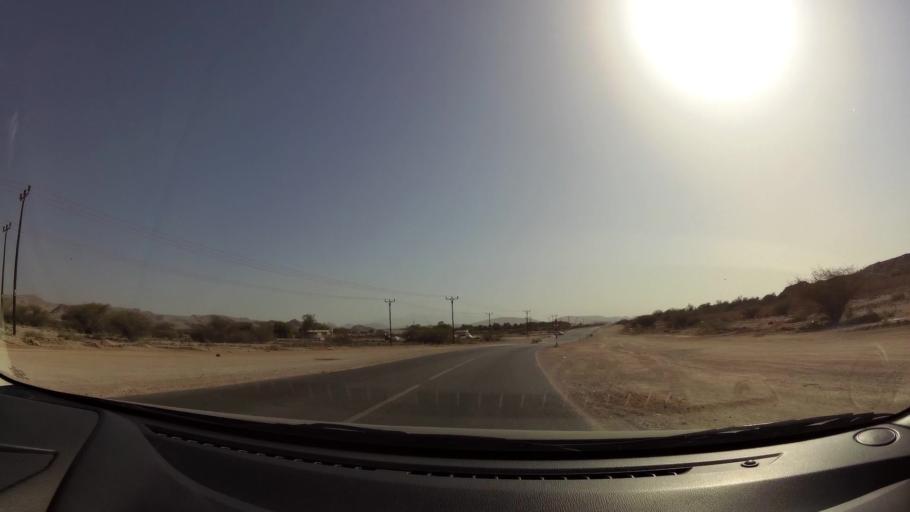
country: OM
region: Muhafazat Masqat
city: As Sib al Jadidah
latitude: 23.5809
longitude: 58.2383
